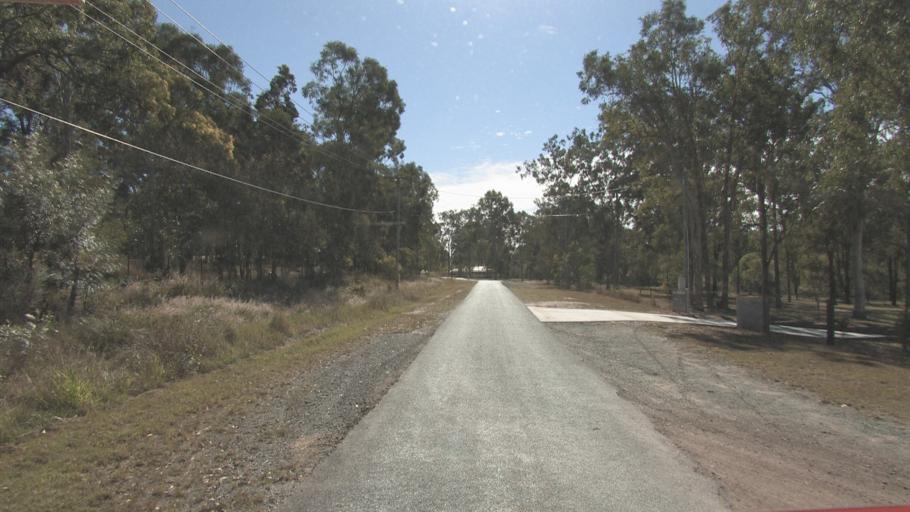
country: AU
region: Queensland
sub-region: Ipswich
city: Springfield Lakes
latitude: -27.7058
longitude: 152.9415
